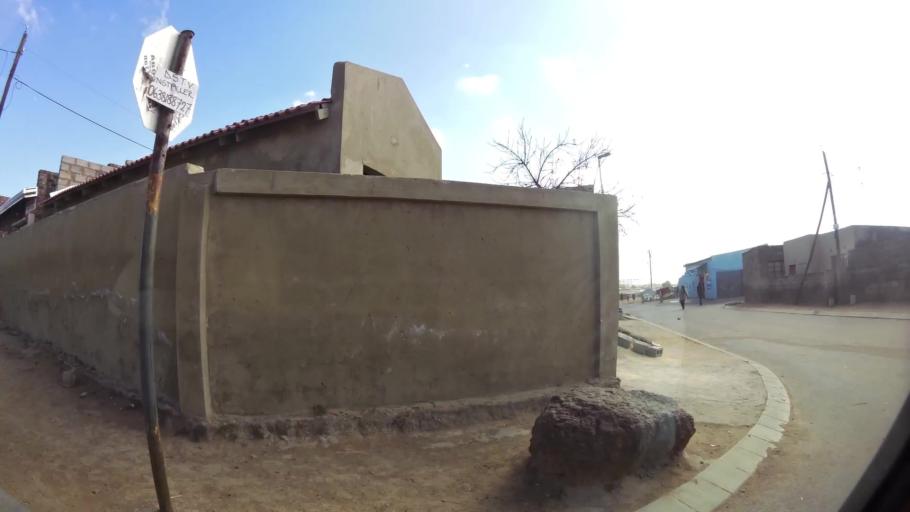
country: ZA
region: Gauteng
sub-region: City of Johannesburg Metropolitan Municipality
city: Modderfontein
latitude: -26.0408
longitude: 28.1795
